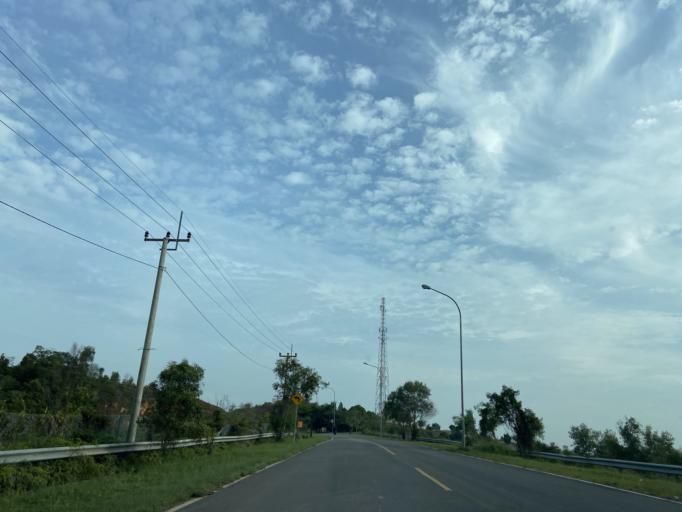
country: ID
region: Riau Islands
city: Tanjungpinang
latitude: 0.9496
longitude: 104.0770
